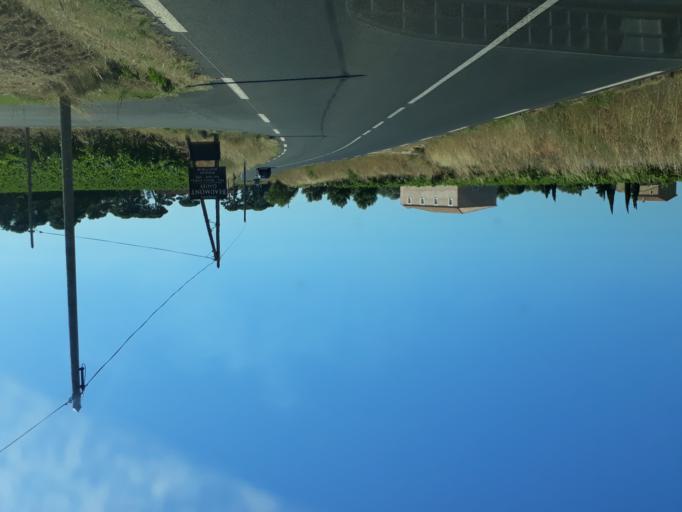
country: FR
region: Languedoc-Roussillon
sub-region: Departement de l'Herault
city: Agde
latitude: 43.3452
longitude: 3.4876
